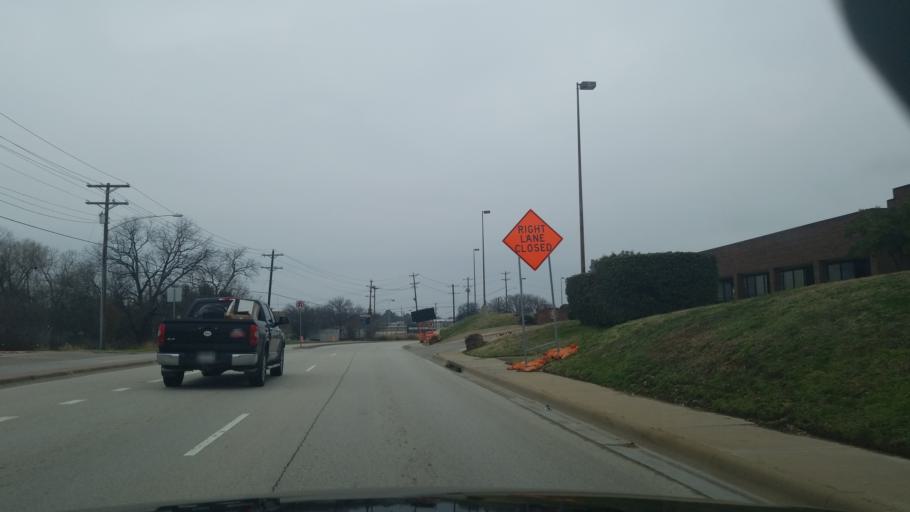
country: US
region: Texas
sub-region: Denton County
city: Denton
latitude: 33.1963
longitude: -97.1240
